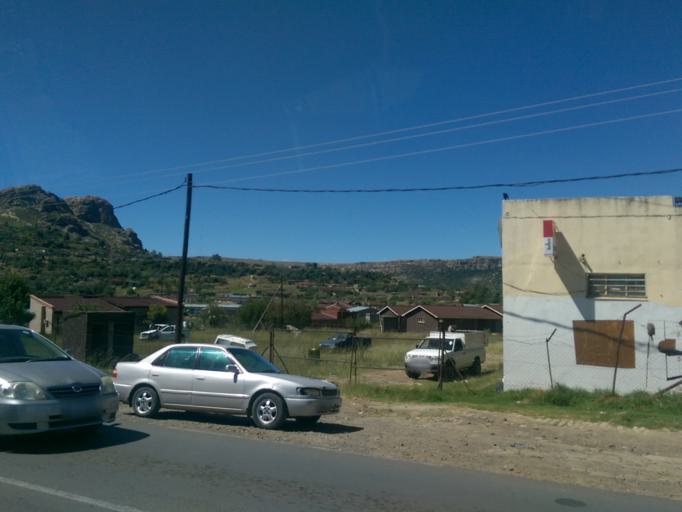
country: LS
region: Maseru
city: Maseru
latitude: -29.3633
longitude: 27.5302
